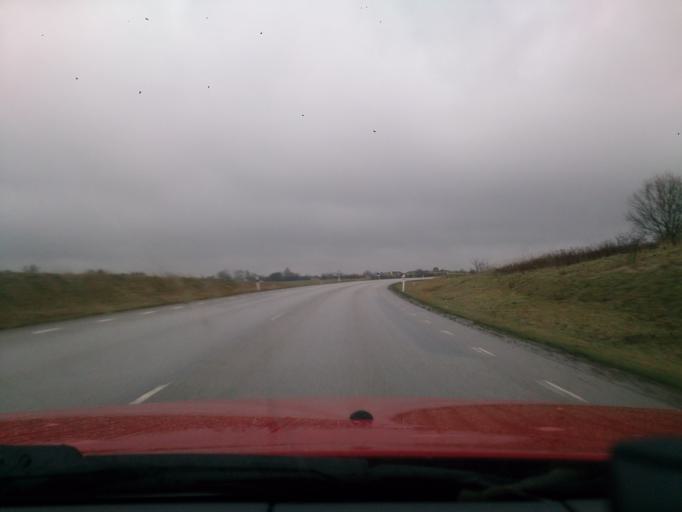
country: SE
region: Skane
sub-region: Ystads Kommun
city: Ystad
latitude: 55.4348
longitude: 13.7798
